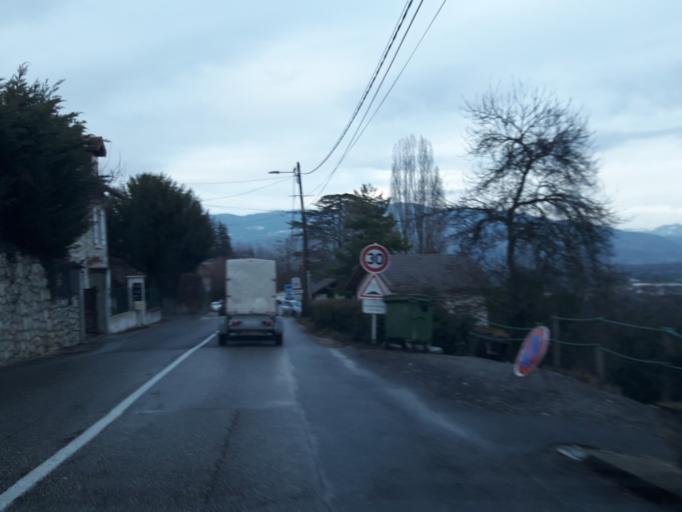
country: FR
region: Rhone-Alpes
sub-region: Departement de la Haute-Savoie
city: Etrembieres
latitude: 46.1617
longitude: 6.2333
